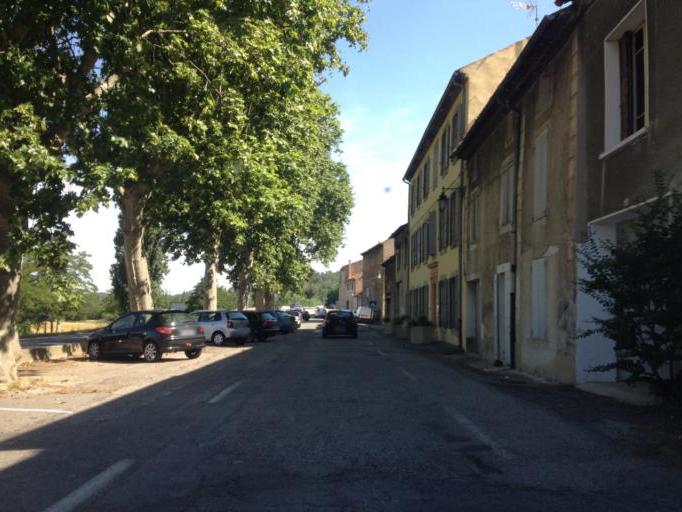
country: FR
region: Provence-Alpes-Cote d'Azur
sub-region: Departement du Vaucluse
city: Mornas
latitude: 44.2054
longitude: 4.7271
